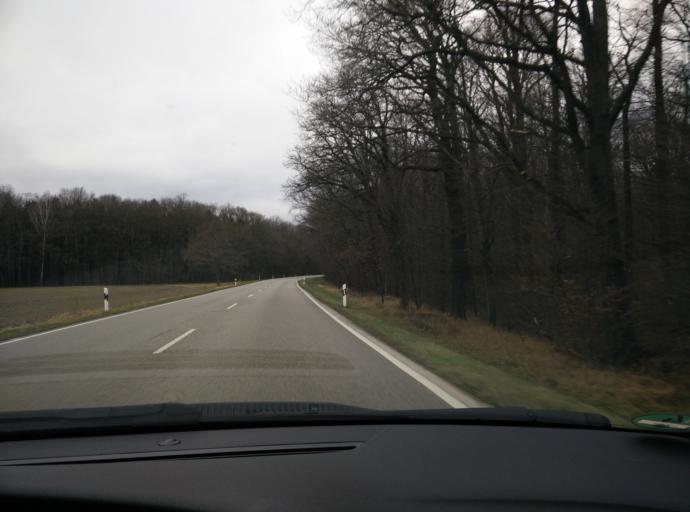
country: DE
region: Saxony
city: Frohburg
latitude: 51.0222
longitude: 12.5566
